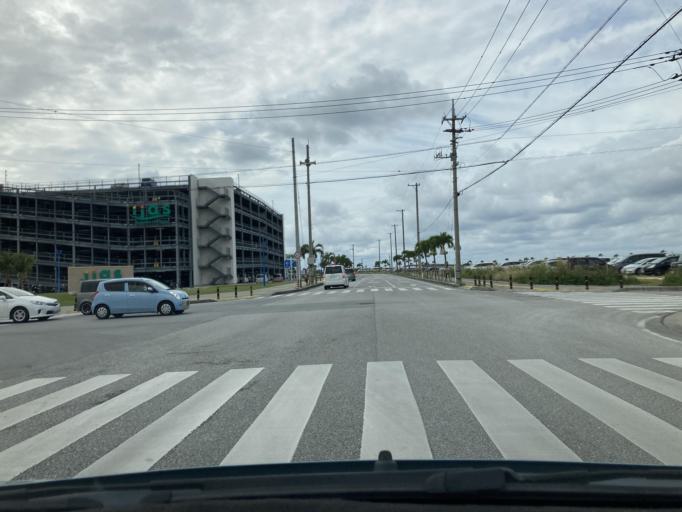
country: JP
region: Okinawa
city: Itoman
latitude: 26.1589
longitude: 127.6523
